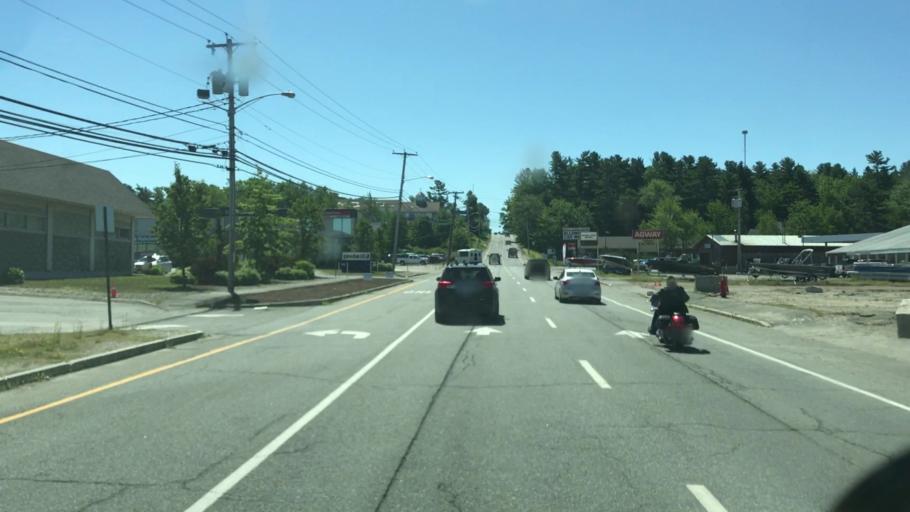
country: US
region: Maine
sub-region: Hancock County
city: Ellsworth
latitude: 44.5309
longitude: -68.4061
